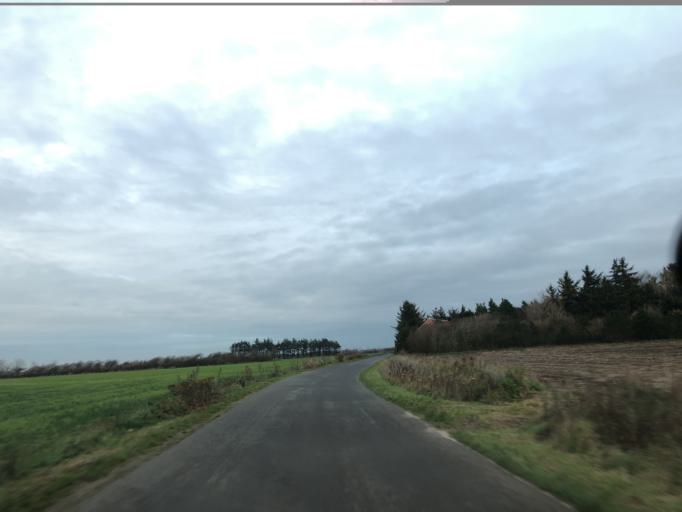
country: DK
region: Central Jutland
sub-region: Holstebro Kommune
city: Ulfborg
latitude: 56.2699
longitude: 8.2539
